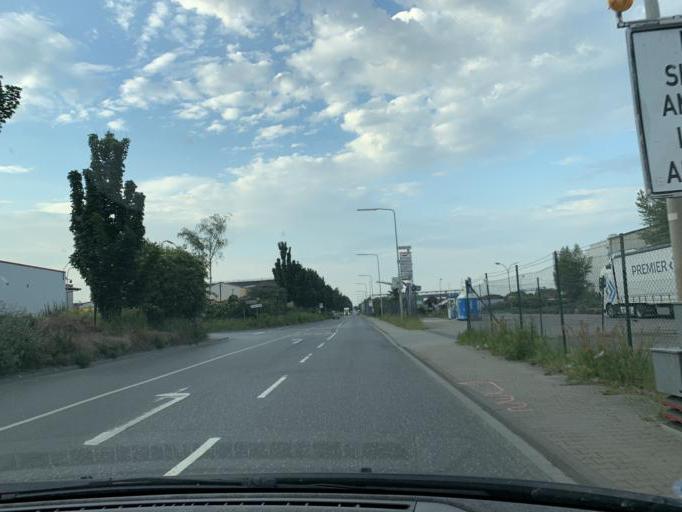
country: DE
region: North Rhine-Westphalia
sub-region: Regierungsbezirk Dusseldorf
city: Dusseldorf
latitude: 51.2143
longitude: 6.7377
